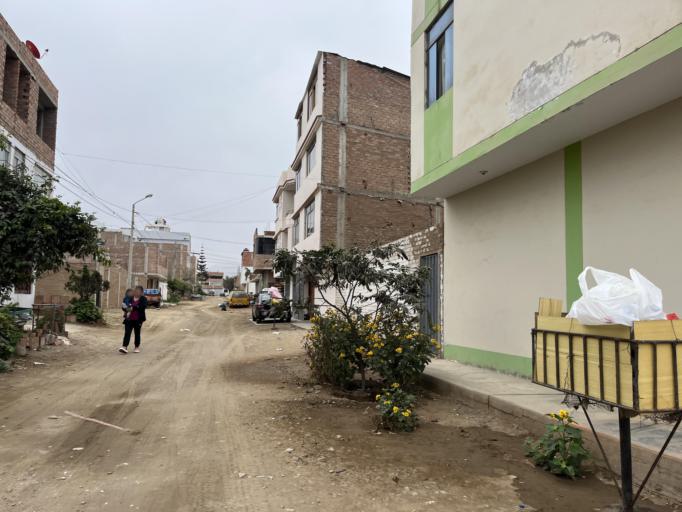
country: PE
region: La Libertad
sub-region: Provincia de Trujillo
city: La Esperanza
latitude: -8.0884
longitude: -79.0518
